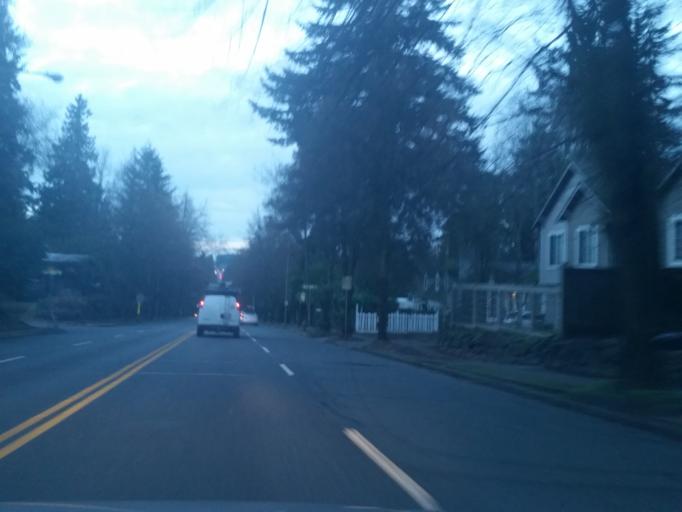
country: US
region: Washington
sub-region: King County
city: Shoreline
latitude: 47.7226
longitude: -122.3126
